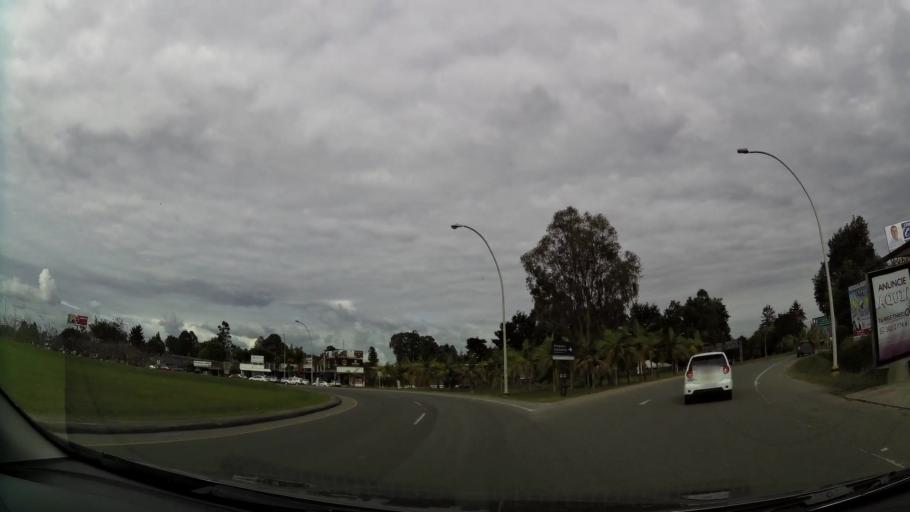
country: CO
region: Antioquia
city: Rionegro
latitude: 6.1754
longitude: -75.4358
